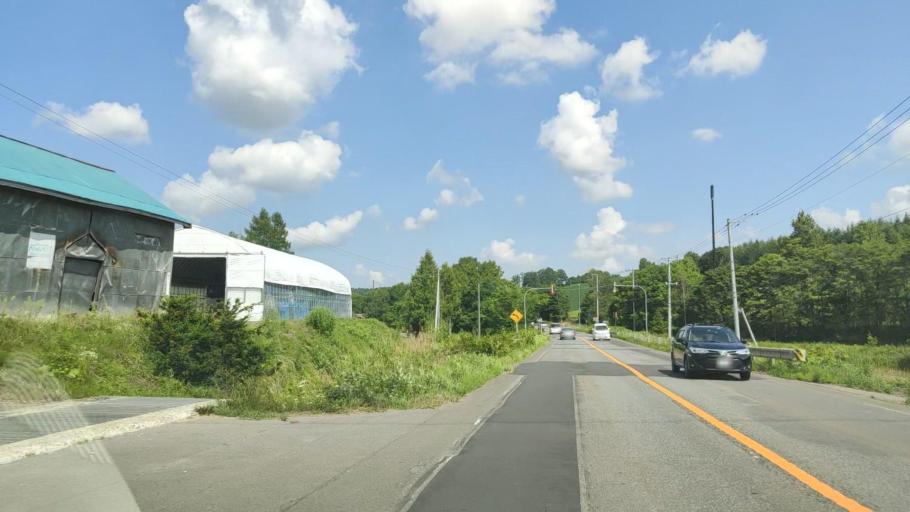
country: JP
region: Hokkaido
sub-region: Asahikawa-shi
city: Asahikawa
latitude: 43.5756
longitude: 142.4395
